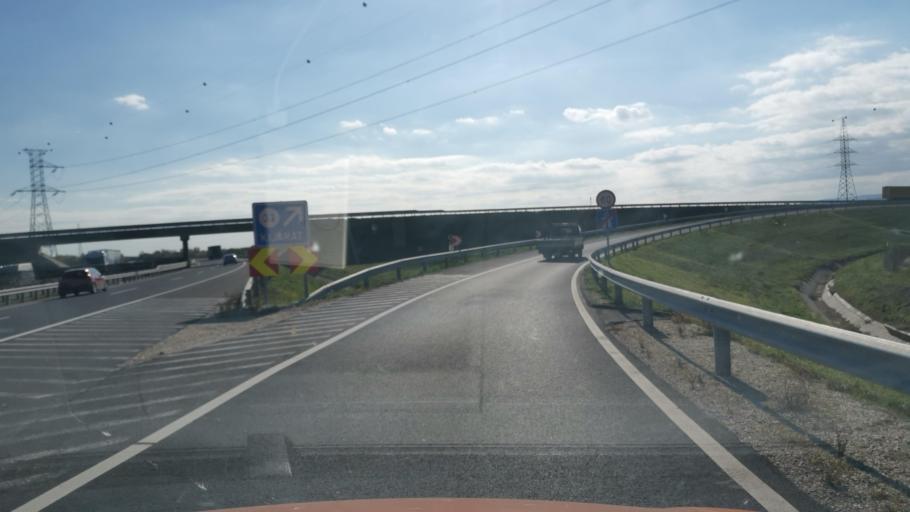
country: HU
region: Borsod-Abauj-Zemplen
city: Arnot
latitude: 48.1369
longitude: 20.8343
